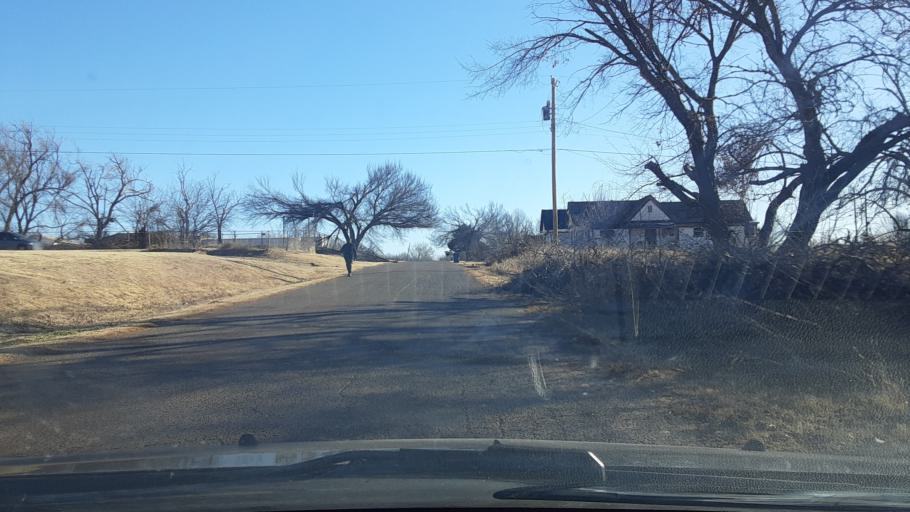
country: US
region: Oklahoma
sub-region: Logan County
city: Guthrie
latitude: 35.8729
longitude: -97.4149
